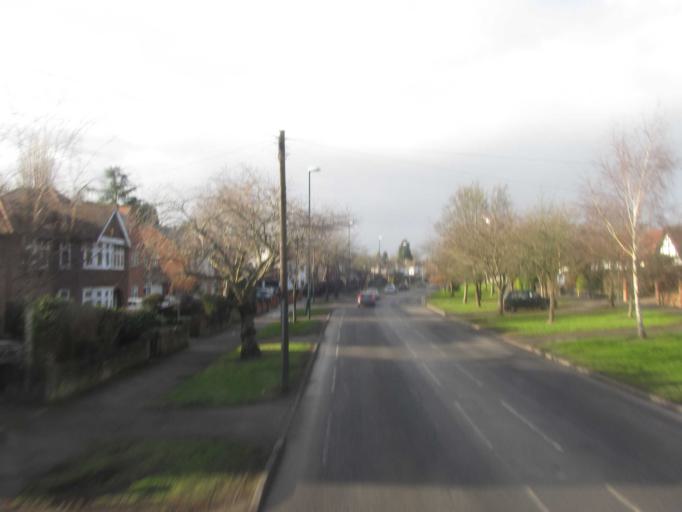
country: GB
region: England
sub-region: Nottinghamshire
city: Kimberley
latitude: 52.9410
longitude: -1.2191
